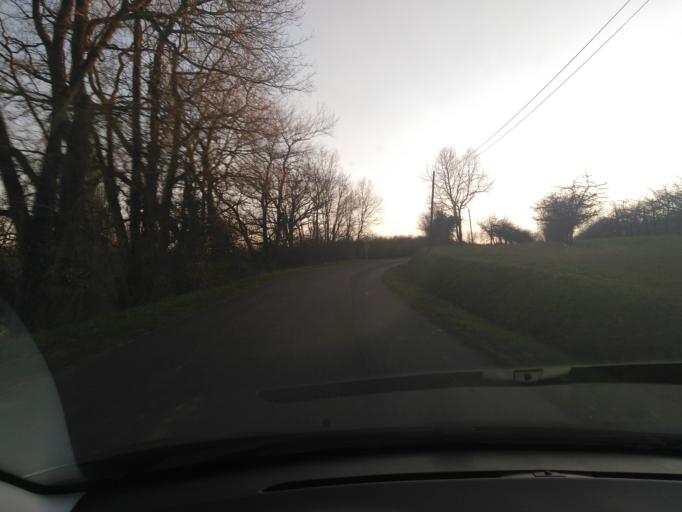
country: FR
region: Aquitaine
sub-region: Departement du Lot-et-Garonne
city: Saint-Hilaire
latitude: 44.5378
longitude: 0.6978
